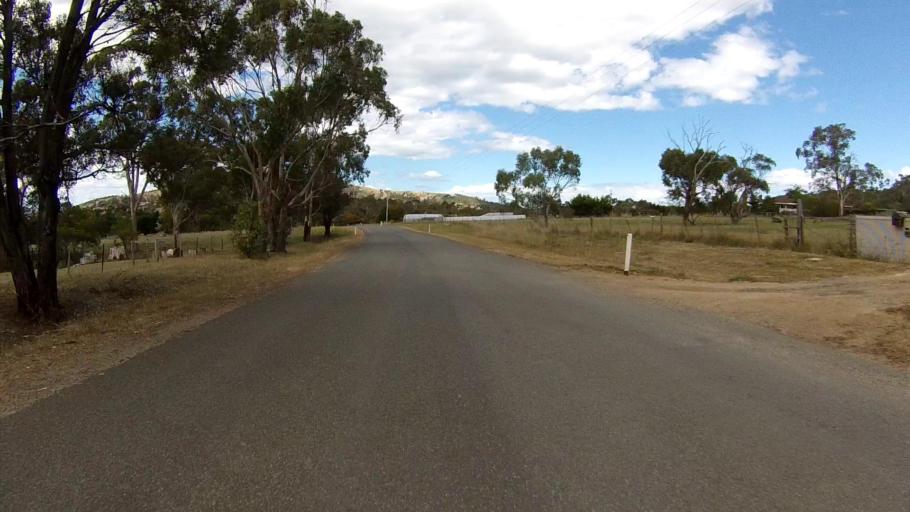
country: AU
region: Tasmania
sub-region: Clarence
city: Acton Park
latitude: -42.8729
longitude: 147.4761
